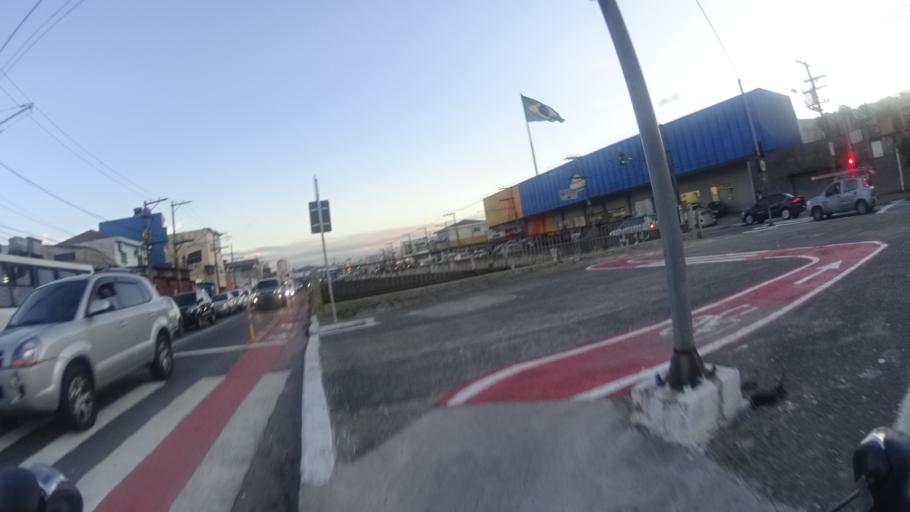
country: BR
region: Sao Paulo
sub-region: Sao Paulo
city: Sao Paulo
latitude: -23.4985
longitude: -46.6638
